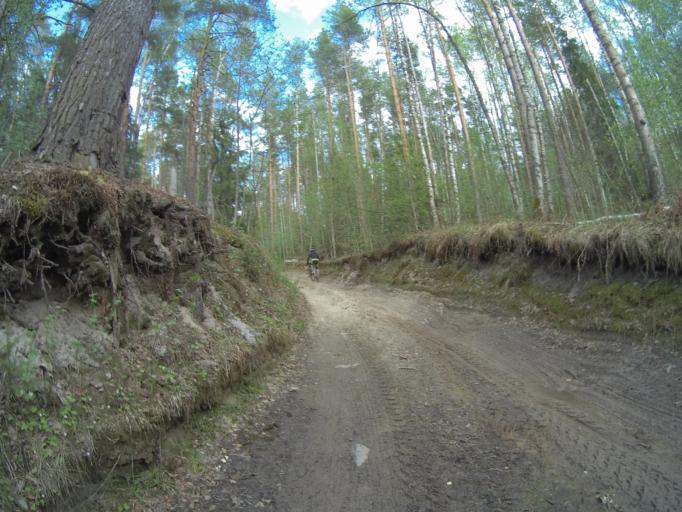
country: RU
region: Vladimir
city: Orgtrud
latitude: 56.1217
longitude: 40.7267
